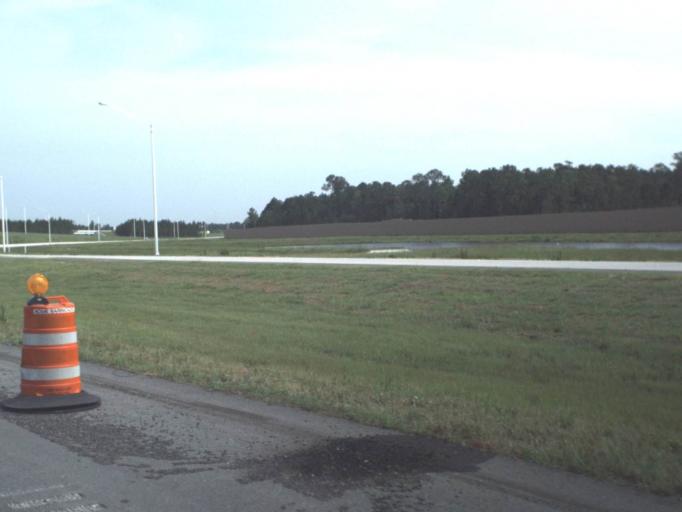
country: US
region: Florida
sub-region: Saint Johns County
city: Fruit Cove
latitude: 30.1123
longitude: -81.5116
